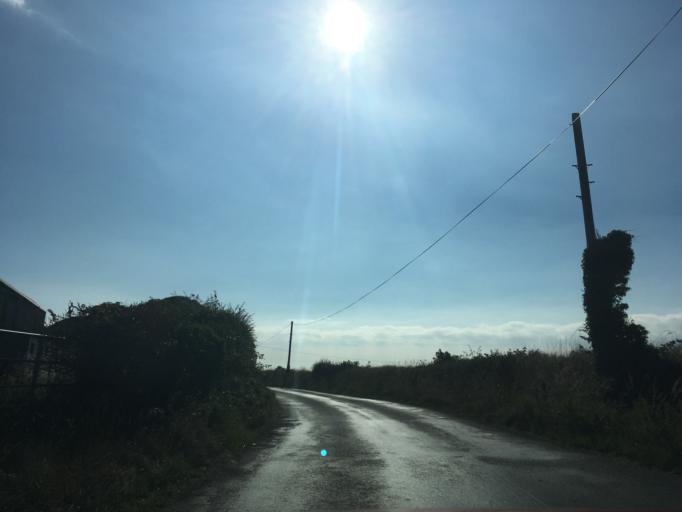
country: IE
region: Leinster
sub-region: Loch Garman
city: Rosslare
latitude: 52.2284
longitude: -6.4369
